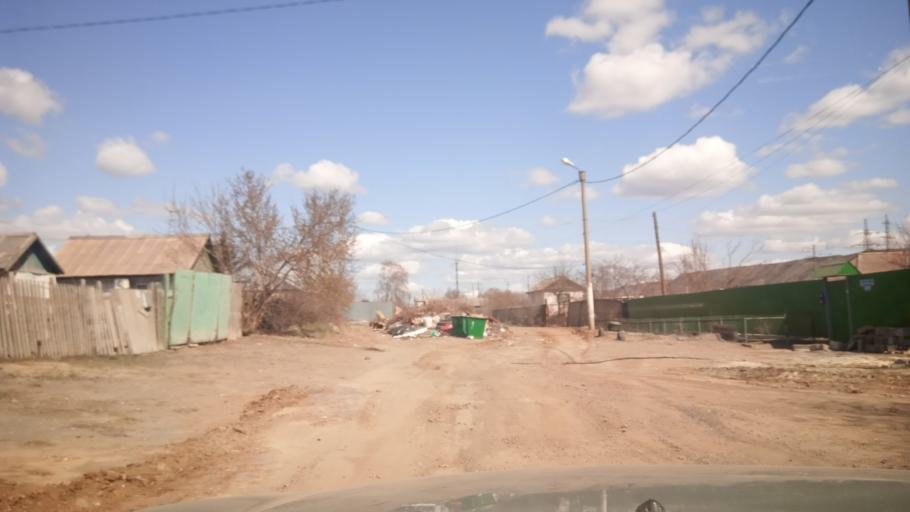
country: RU
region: Orenburg
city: Novotroitsk
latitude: 51.2133
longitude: 58.3169
